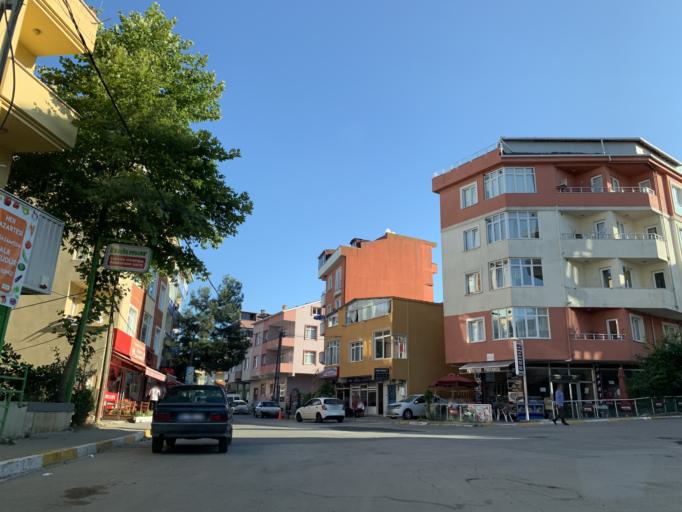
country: TR
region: Istanbul
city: Pendik
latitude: 40.8925
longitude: 29.2584
